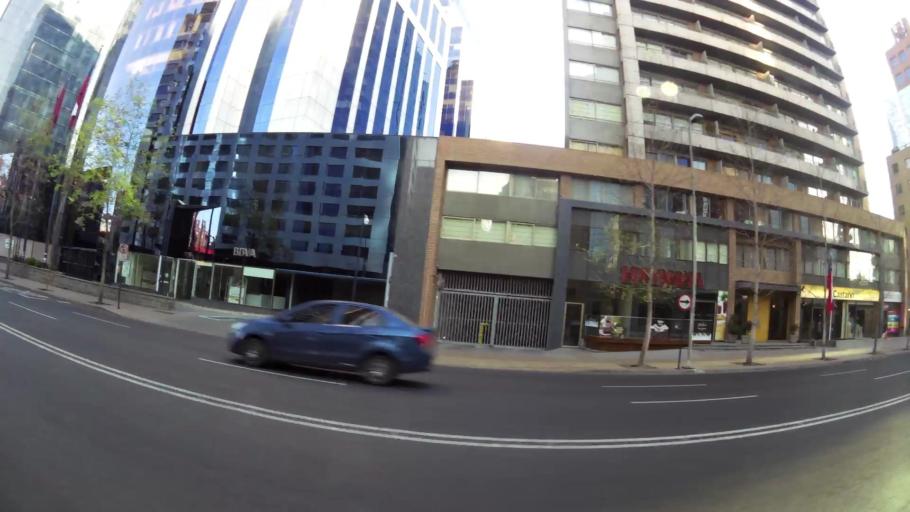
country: CL
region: Santiago Metropolitan
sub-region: Provincia de Santiago
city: Villa Presidente Frei, Nunoa, Santiago, Chile
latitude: -33.4153
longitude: -70.6041
